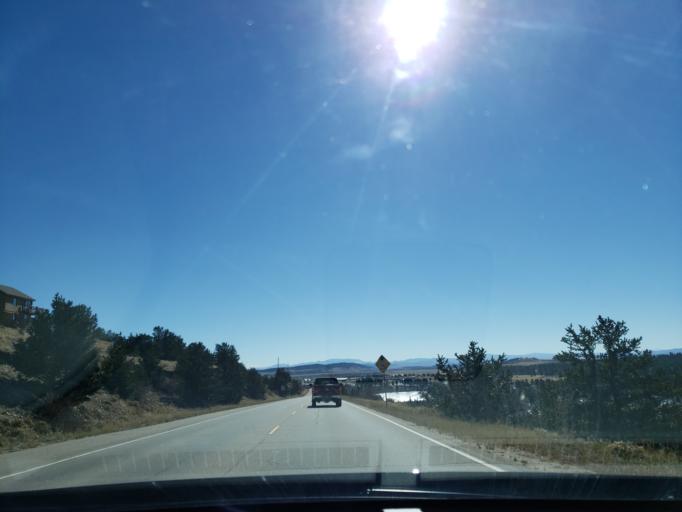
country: US
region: Colorado
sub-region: Park County
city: Fairplay
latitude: 39.2293
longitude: -106.0097
